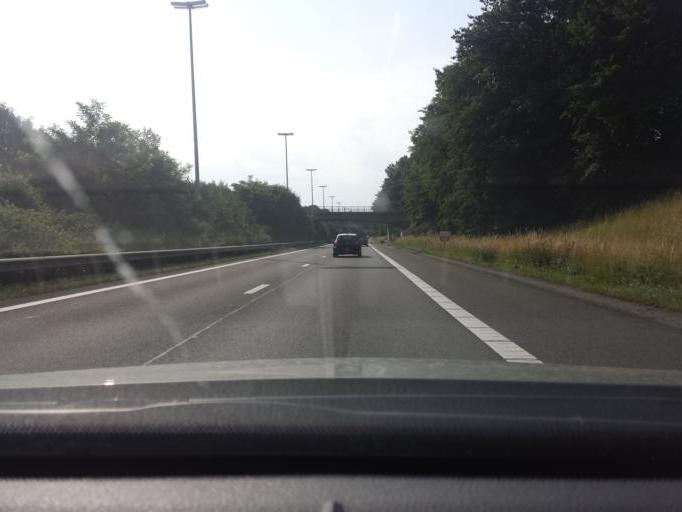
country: BE
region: Flanders
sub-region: Provincie Limburg
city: Hoeselt
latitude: 50.8741
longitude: 5.4788
